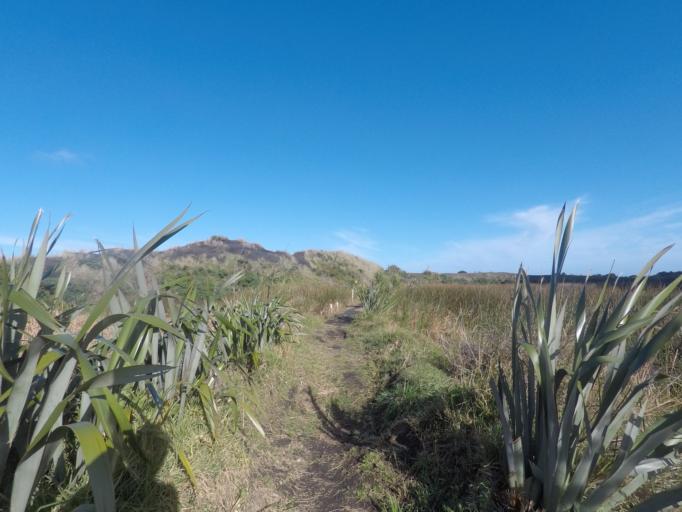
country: NZ
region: Auckland
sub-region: Auckland
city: Titirangi
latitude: -37.0103
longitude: 174.4862
